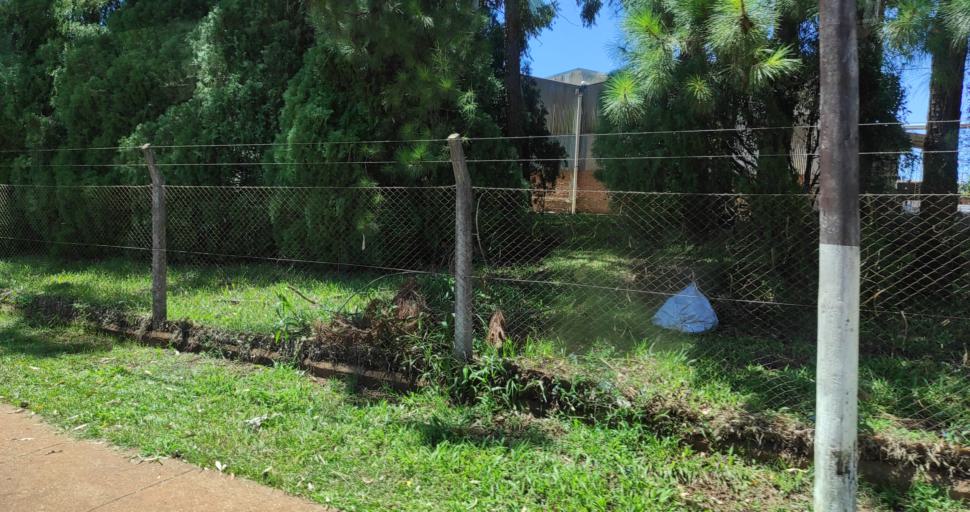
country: AR
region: Misiones
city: Dos de Mayo
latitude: -27.0060
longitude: -54.4785
